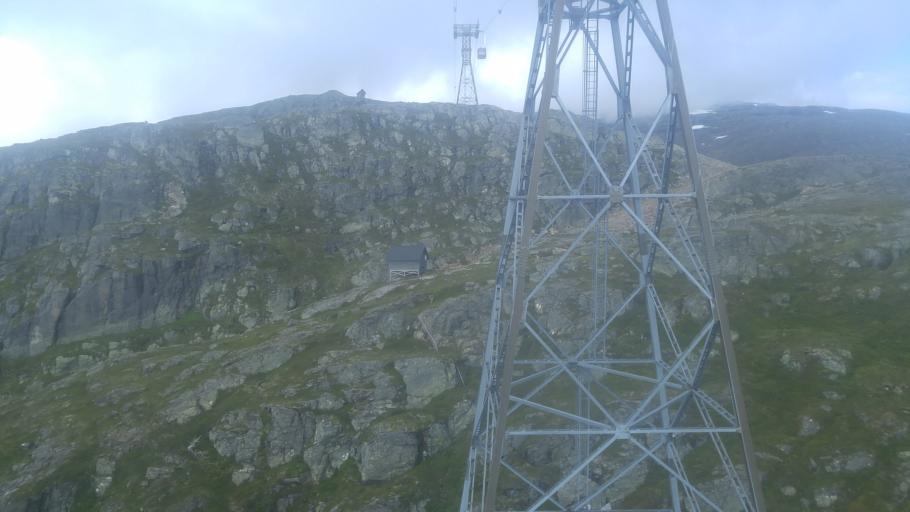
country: SE
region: Jaemtland
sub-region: Are Kommun
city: Are
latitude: 63.4135
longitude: 13.0776
